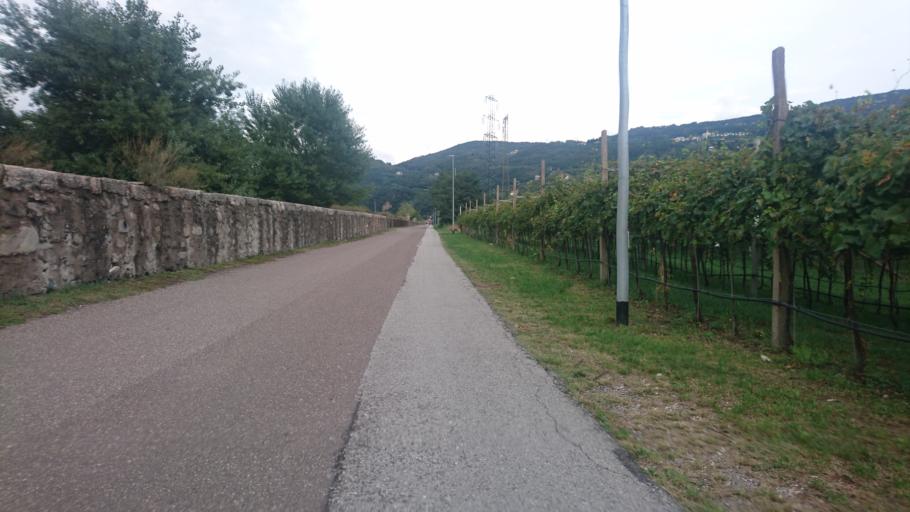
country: IT
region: Trentino-Alto Adige
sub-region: Provincia di Trento
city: Lavis
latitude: 46.1329
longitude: 11.1048
